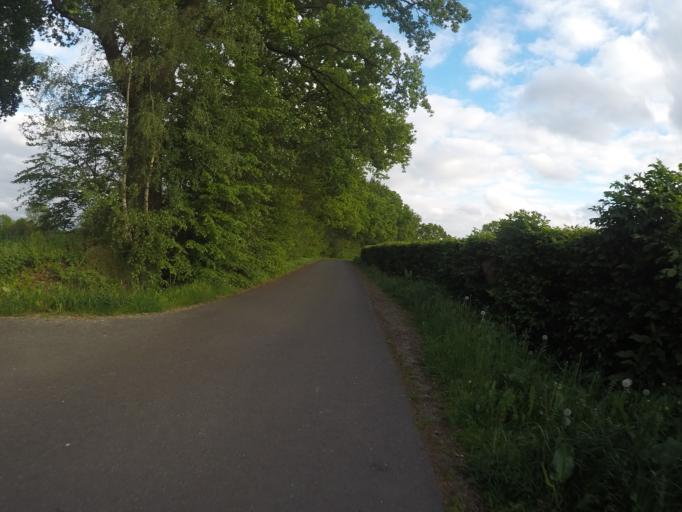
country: DE
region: Schleswig-Holstein
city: Bonningstedt
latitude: 53.6652
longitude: 9.9266
